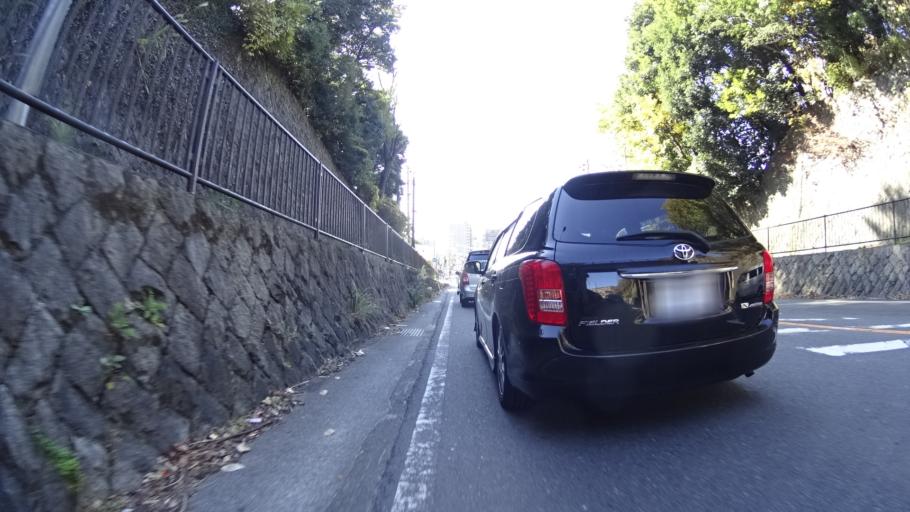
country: JP
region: Kanagawa
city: Zama
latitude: 35.5617
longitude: 139.3593
